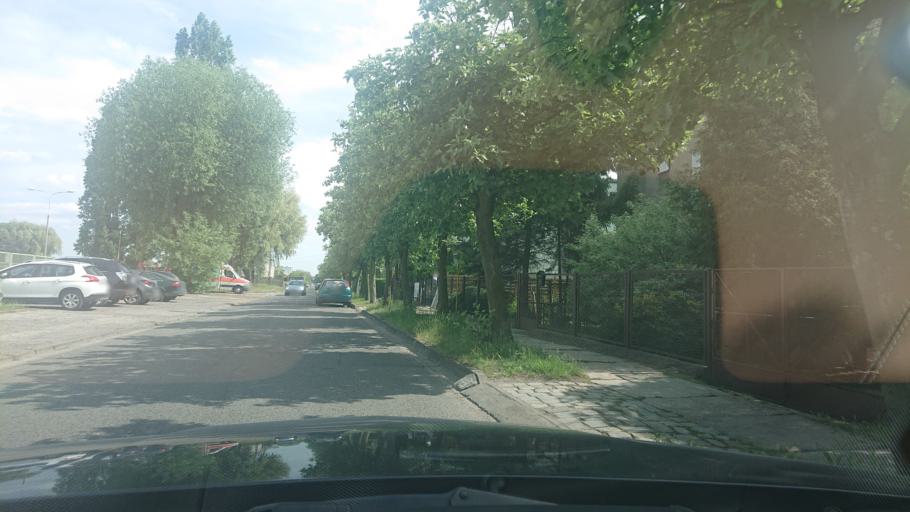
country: PL
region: Greater Poland Voivodeship
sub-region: Powiat gnieznienski
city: Gniezno
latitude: 52.5251
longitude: 17.6045
